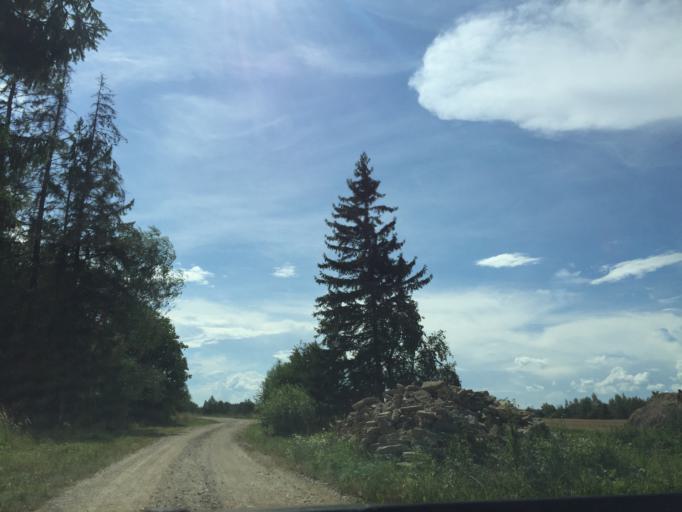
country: LT
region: Siauliu apskritis
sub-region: Joniskis
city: Joniskis
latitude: 56.3011
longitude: 23.6463
